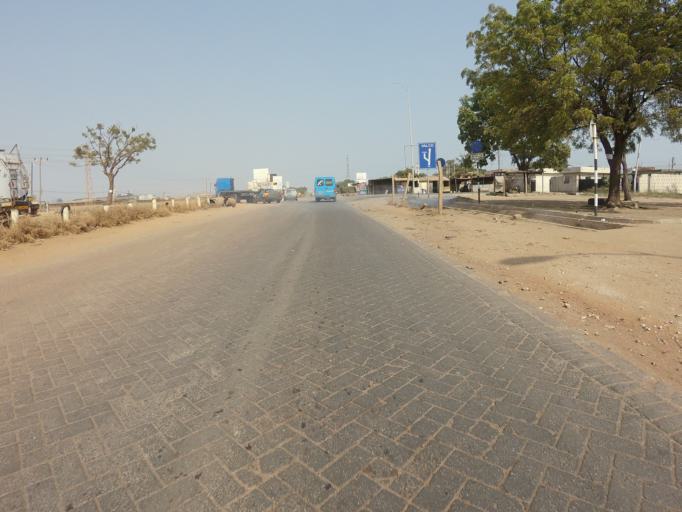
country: GH
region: Greater Accra
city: Tema
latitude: 5.6663
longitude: 0.0090
